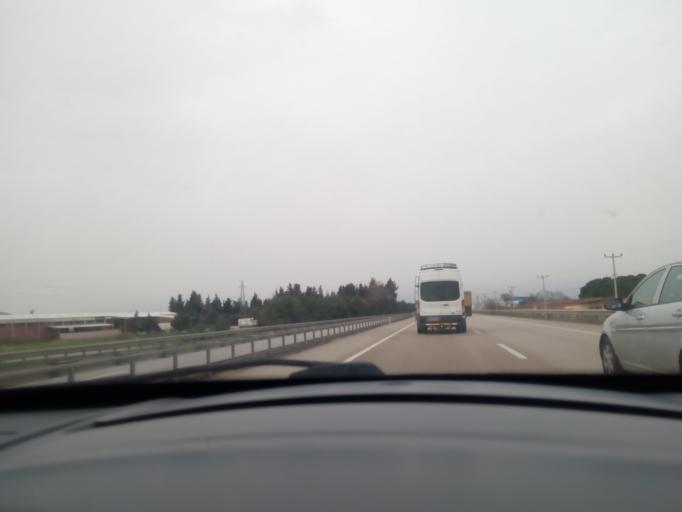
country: TR
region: Bursa
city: Tatkavakli
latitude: 40.0319
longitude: 28.3547
